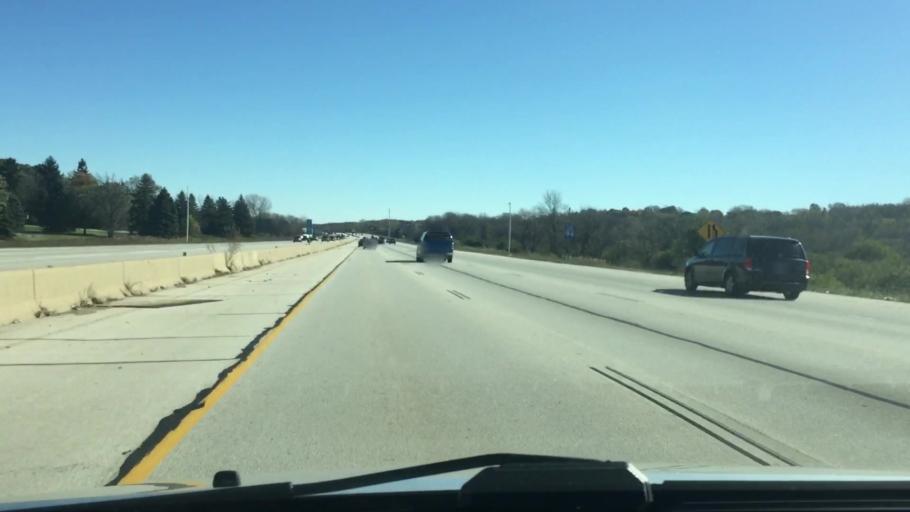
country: US
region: Wisconsin
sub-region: Waukesha County
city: Brookfield
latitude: 43.0316
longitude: -88.1606
